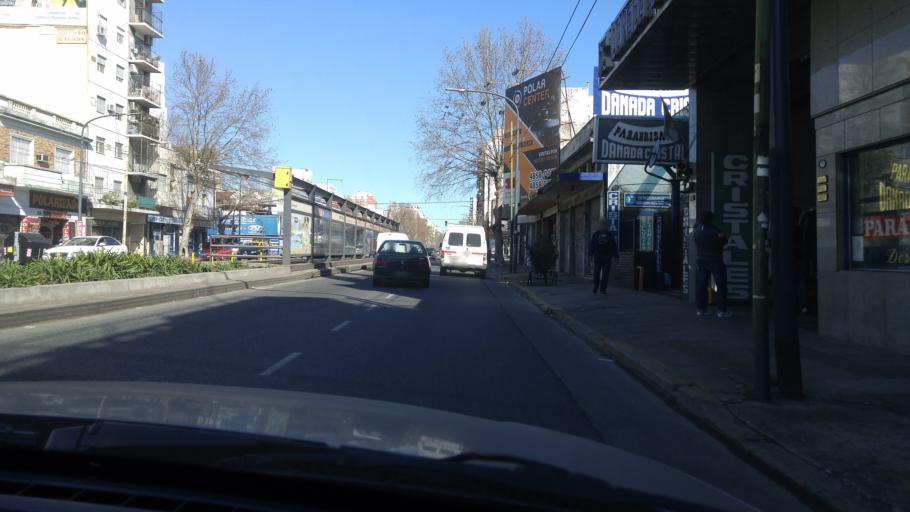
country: AR
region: Buenos Aires F.D.
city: Colegiales
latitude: -34.5996
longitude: -58.4514
